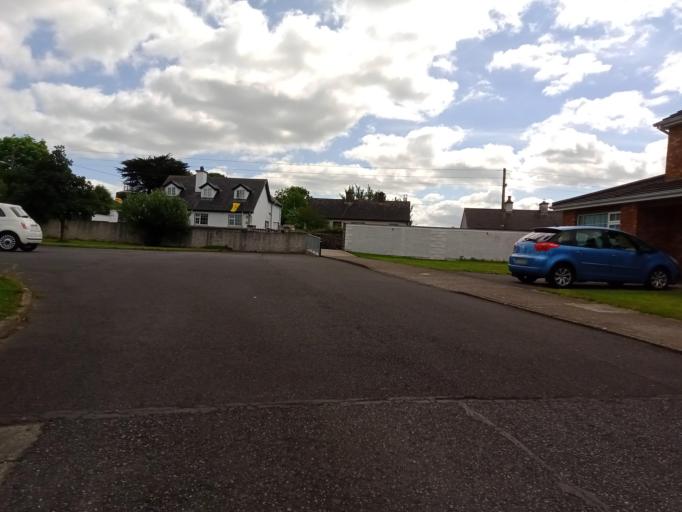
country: IE
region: Leinster
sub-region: Kilkenny
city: Callan
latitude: 52.5433
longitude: -7.3933
